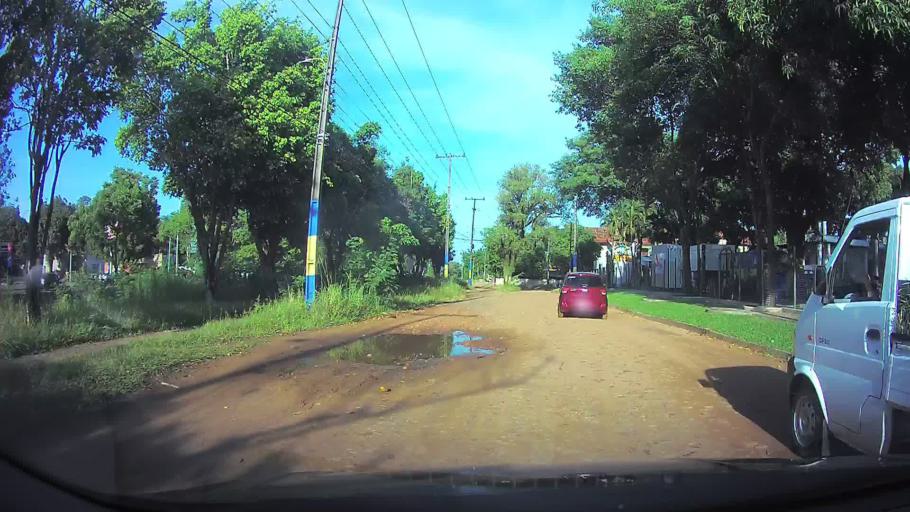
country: PY
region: Central
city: San Lorenzo
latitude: -25.2639
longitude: -57.5078
